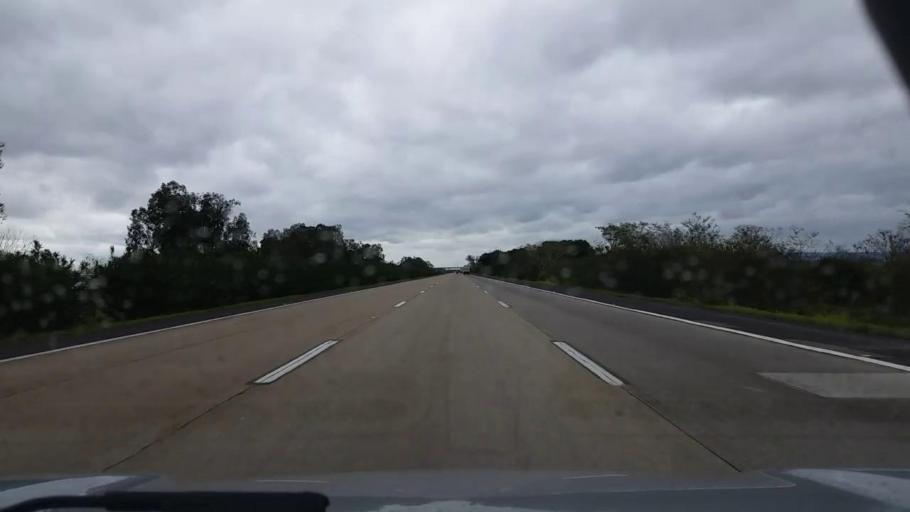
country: BR
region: Rio Grande do Sul
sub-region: Rolante
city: Rolante
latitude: -29.8863
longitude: -50.6447
